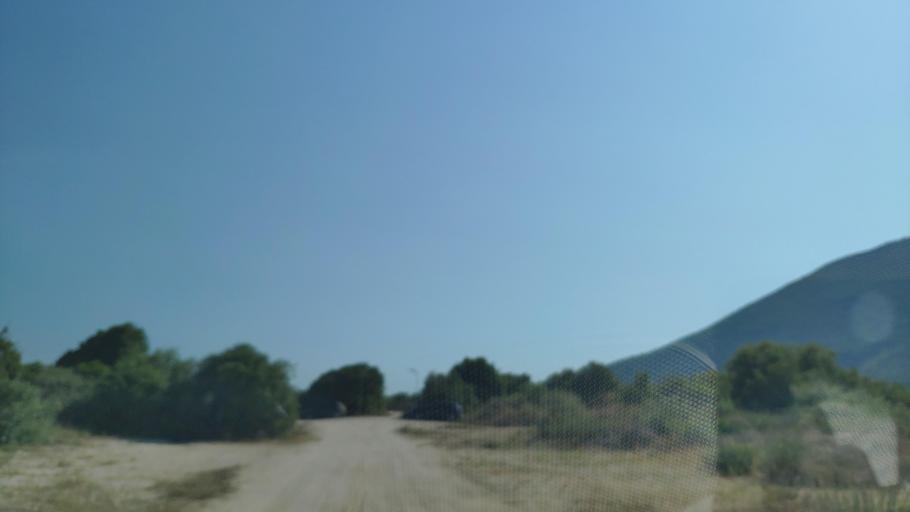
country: GR
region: Ionian Islands
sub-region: Lefkada
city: Lefkada
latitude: 38.8502
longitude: 20.7369
